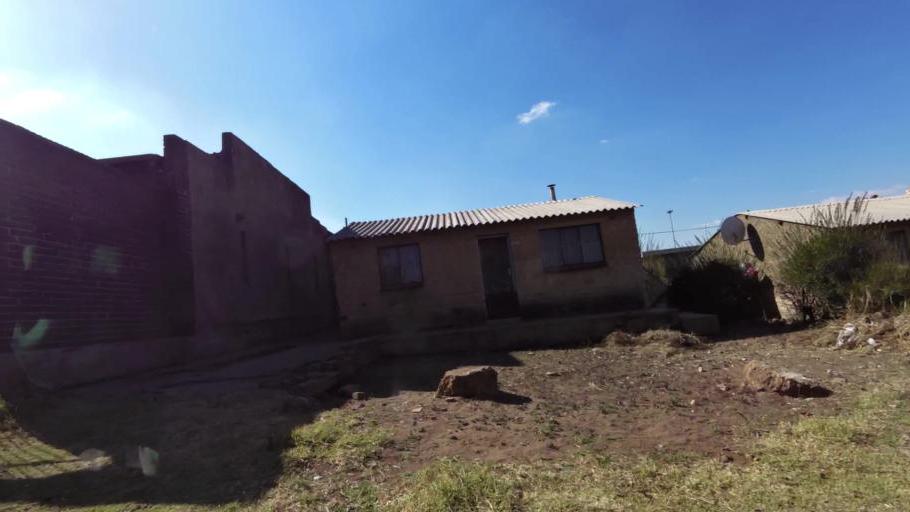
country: ZA
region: Gauteng
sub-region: City of Johannesburg Metropolitan Municipality
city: Soweto
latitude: -26.2430
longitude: 27.9059
